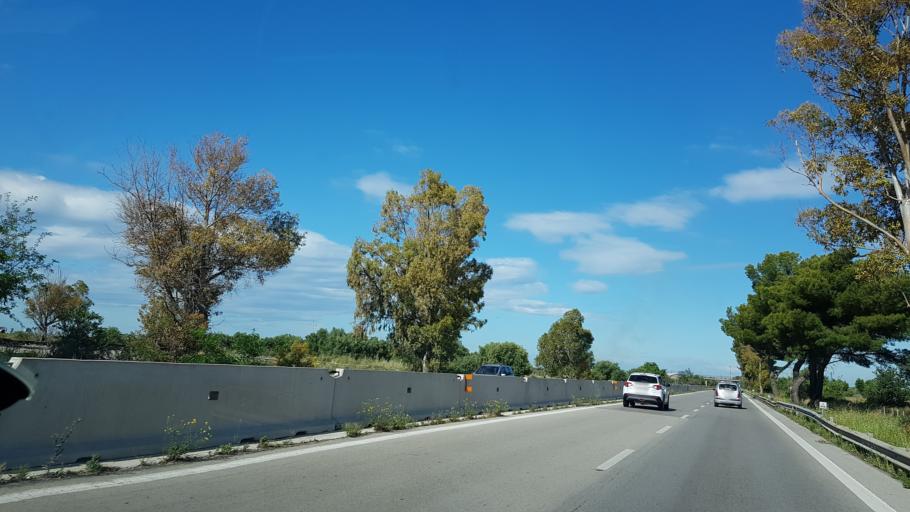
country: IT
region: Apulia
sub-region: Provincia di Taranto
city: Paolo VI
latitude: 40.5145
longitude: 17.3080
